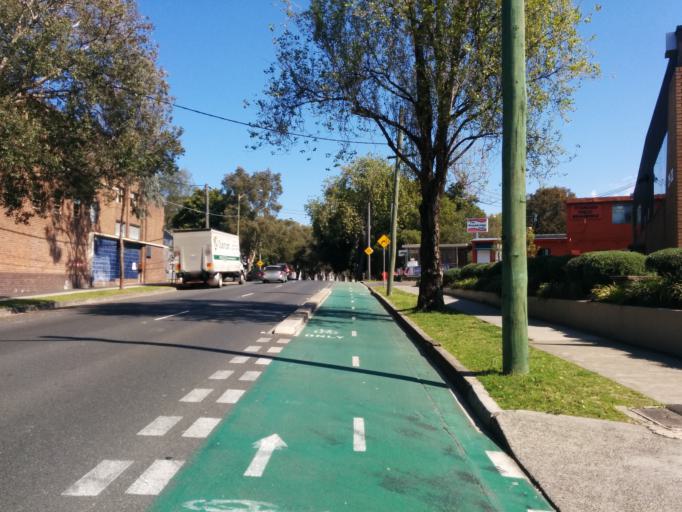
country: AU
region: New South Wales
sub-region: City of Sydney
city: Alexandria
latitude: -33.9076
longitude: 151.1977
